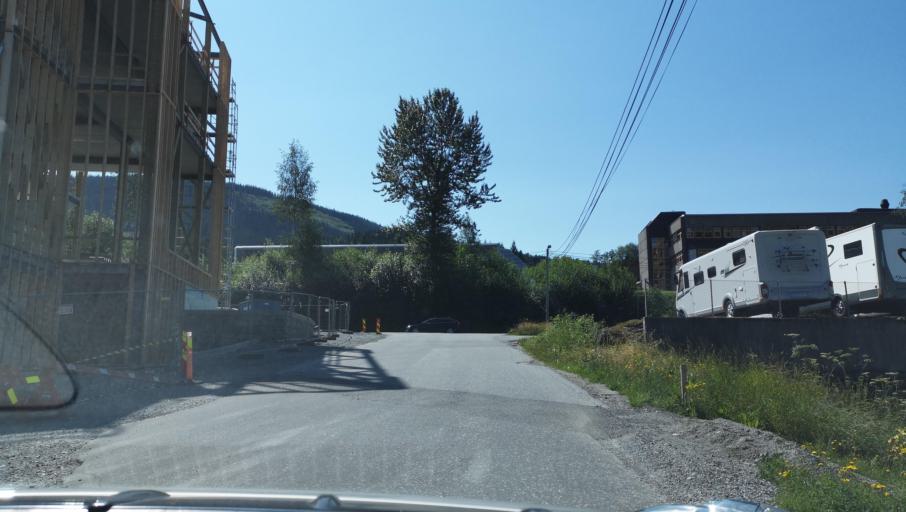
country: NO
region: Hordaland
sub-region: Voss
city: Voss
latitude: 60.6352
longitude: 6.4590
